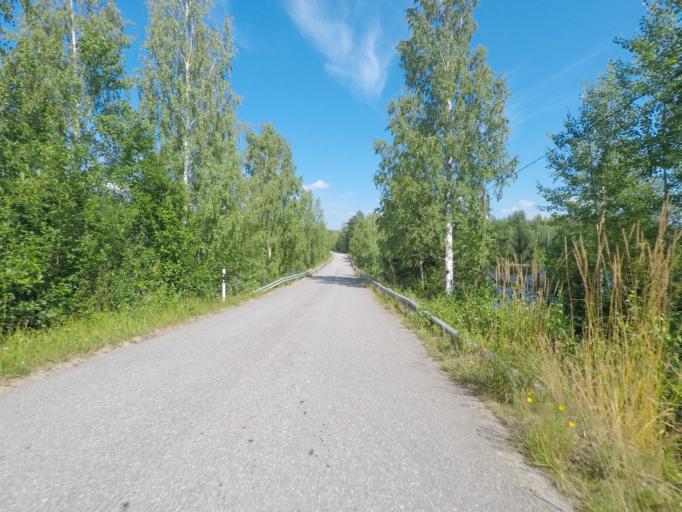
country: FI
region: Southern Savonia
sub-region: Mikkeli
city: Puumala
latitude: 61.4078
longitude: 28.0874
